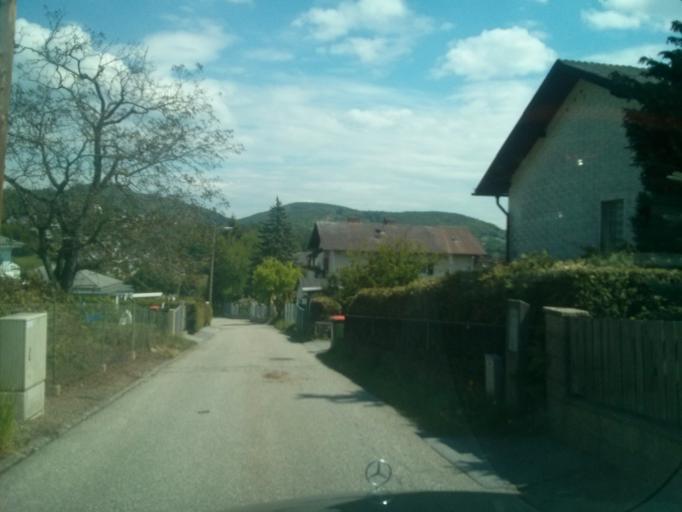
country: AT
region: Styria
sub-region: Politischer Bezirk Graz-Umgebung
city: Stattegg
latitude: 47.1240
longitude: 15.4200
